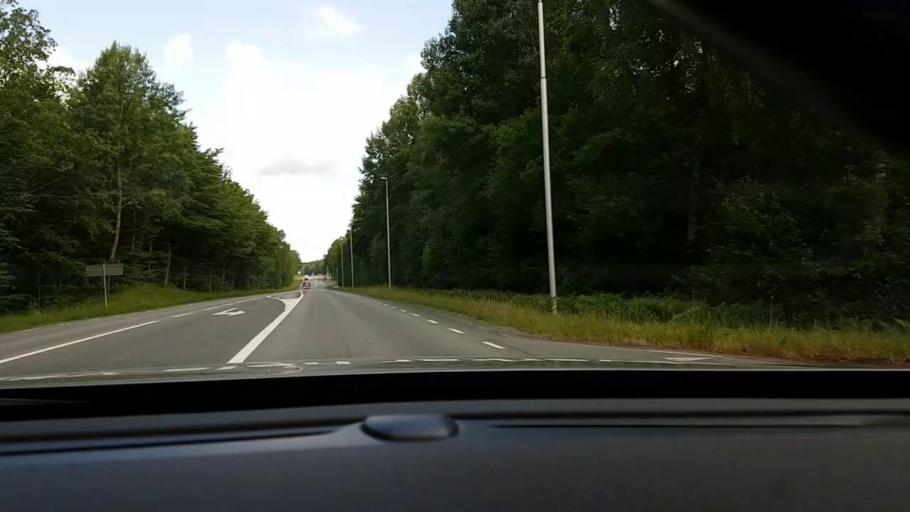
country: SE
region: Skane
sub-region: Hassleholms Kommun
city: Hassleholm
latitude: 56.1608
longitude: 13.7394
